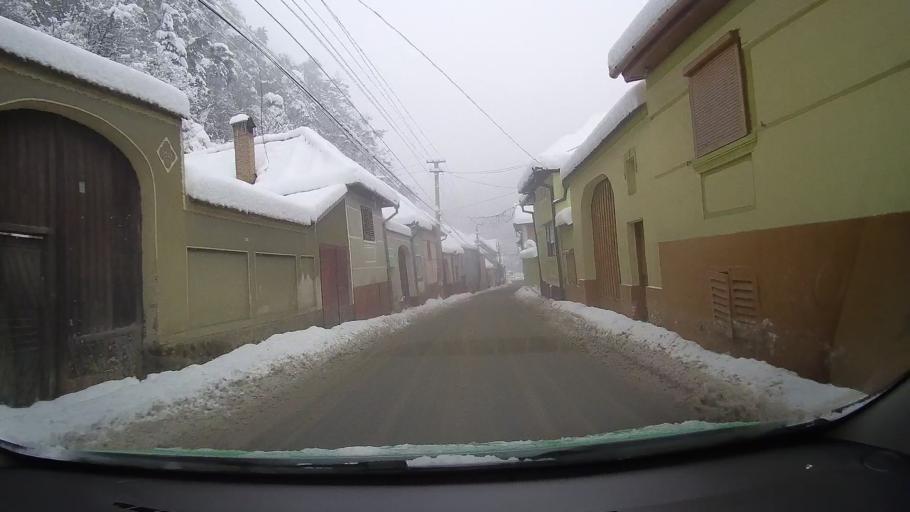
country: RO
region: Sibiu
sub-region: Comuna Tilisca
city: Tilisca
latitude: 45.8003
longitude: 23.8435
